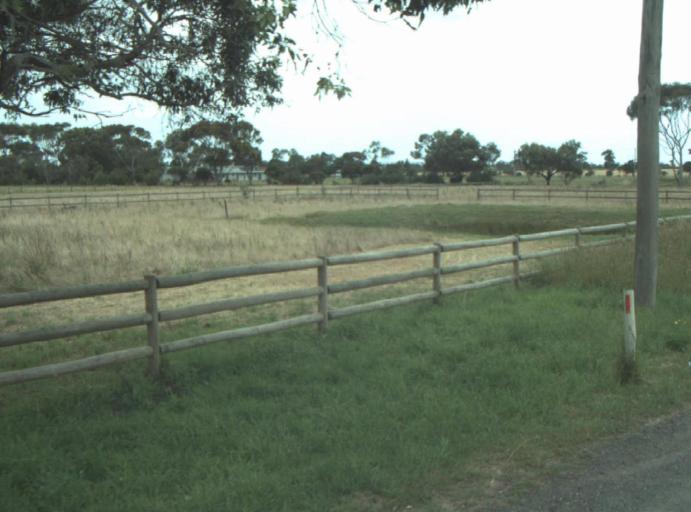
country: AU
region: Victoria
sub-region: Greater Geelong
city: Leopold
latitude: -38.1793
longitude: 144.4201
